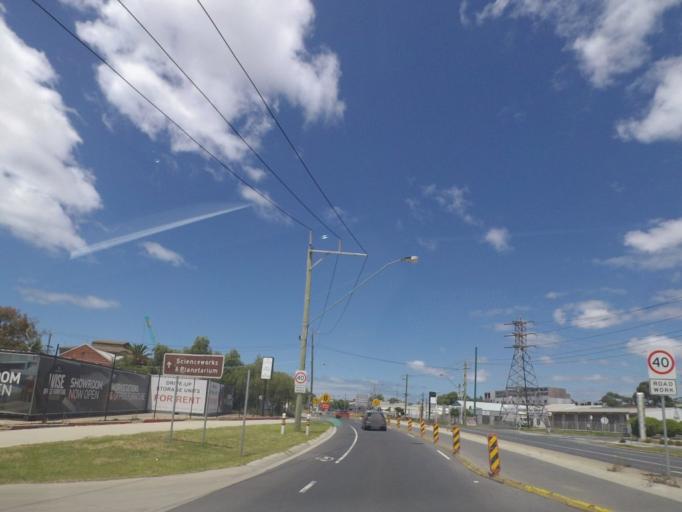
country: AU
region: Victoria
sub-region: Maribyrnong
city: Yarraville
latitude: -37.8086
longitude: 144.9029
